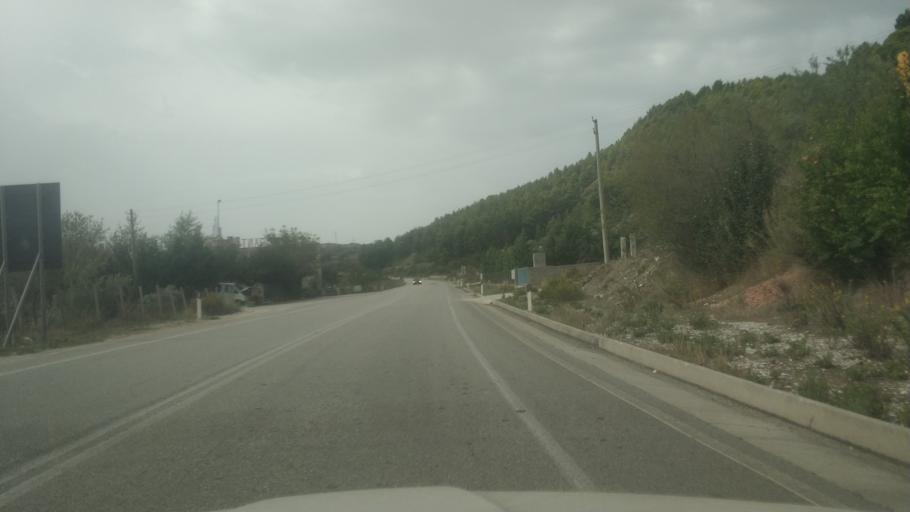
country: AL
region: Gjirokaster
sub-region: Rrethi i Tepelenes
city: Memaliaj
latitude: 40.3535
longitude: 19.9511
